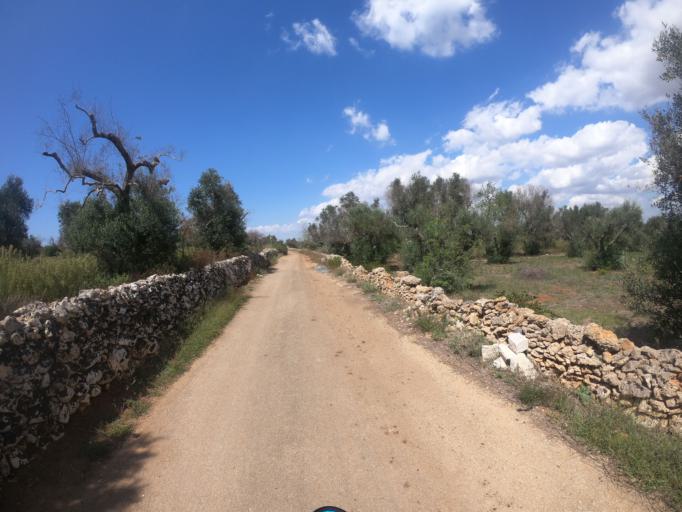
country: IT
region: Apulia
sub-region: Provincia di Lecce
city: Secli
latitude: 40.1162
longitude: 18.0874
